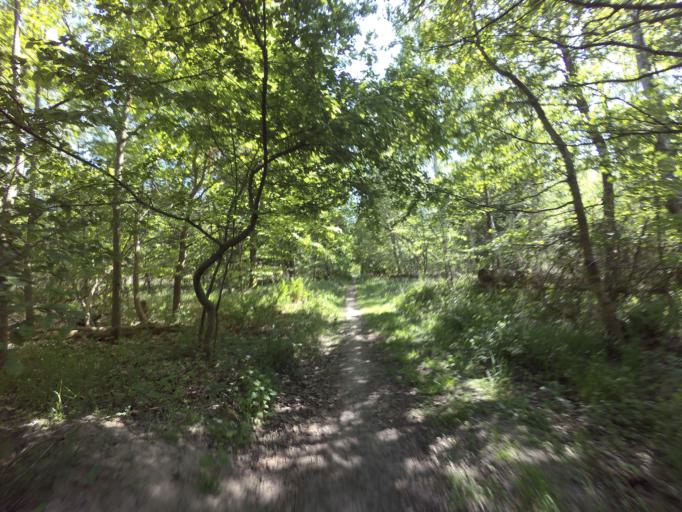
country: DE
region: Lower Saxony
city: Lehre
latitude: 52.3161
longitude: 10.6543
